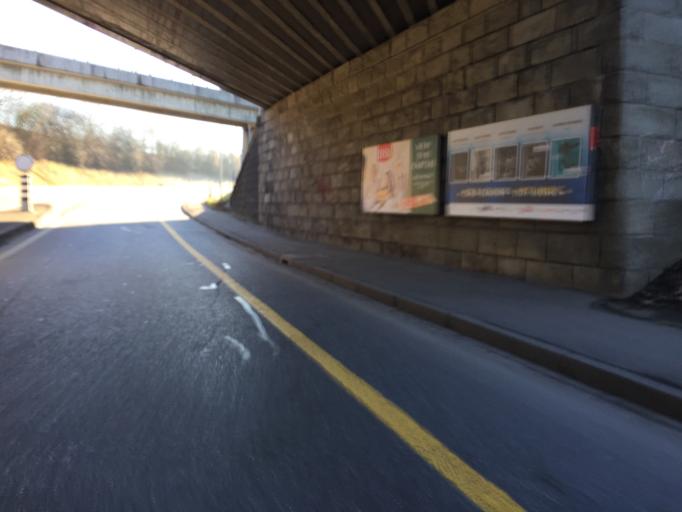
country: CH
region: Bern
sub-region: Bern-Mittelland District
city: Rubigen
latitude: 46.8924
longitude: 7.5493
